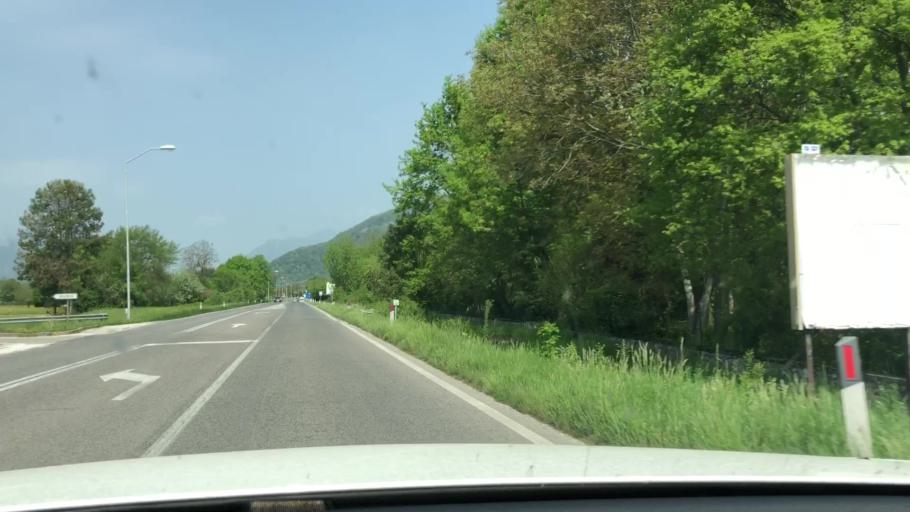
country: IT
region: Friuli Venezia Giulia
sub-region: Provincia di Udine
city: Magnano in Riviera
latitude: 46.2100
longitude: 13.1856
